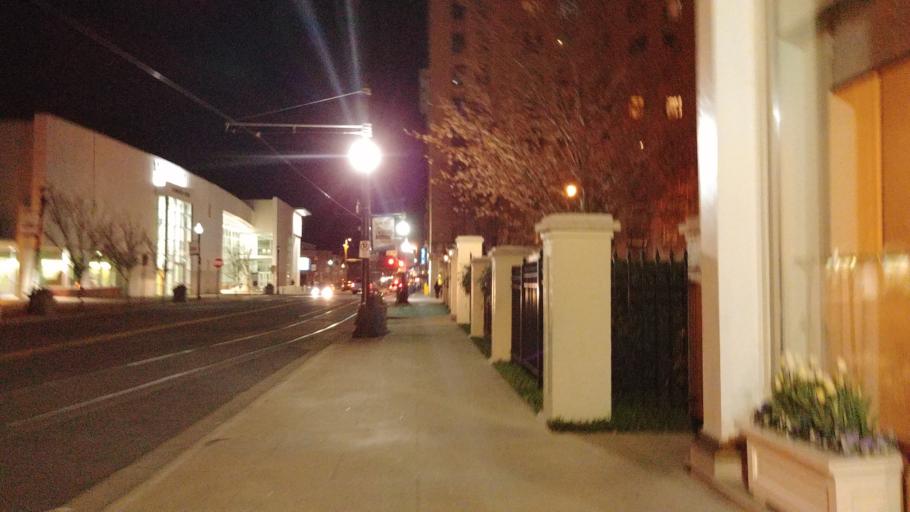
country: US
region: Arkansas
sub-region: Pulaski County
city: Little Rock
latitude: 34.7482
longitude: -92.2711
